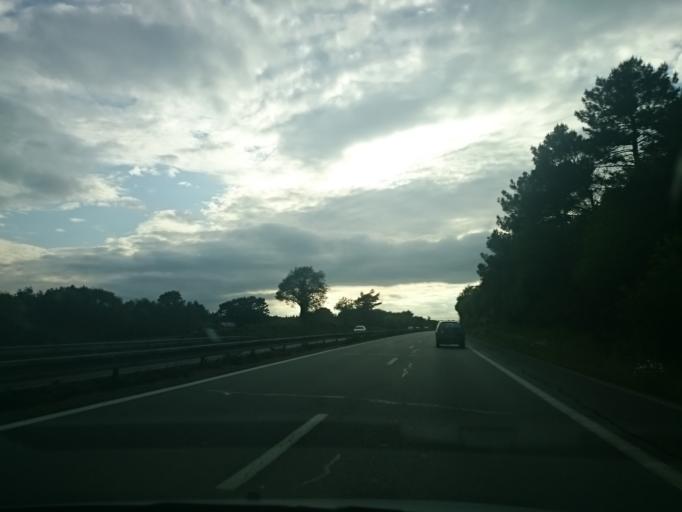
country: FR
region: Brittany
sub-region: Departement du Morbihan
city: Nostang
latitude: 47.7684
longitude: -3.1661
